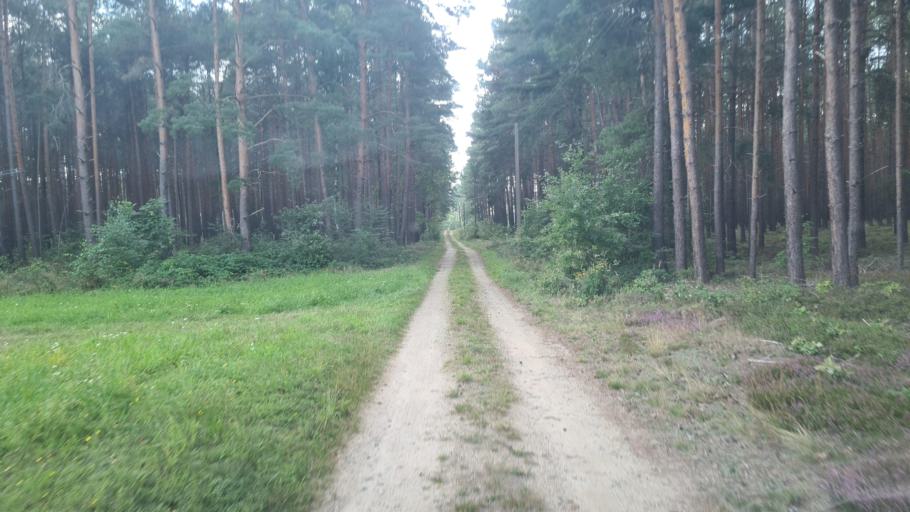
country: DE
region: Brandenburg
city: Schonewalde
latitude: 51.7457
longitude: 13.5975
